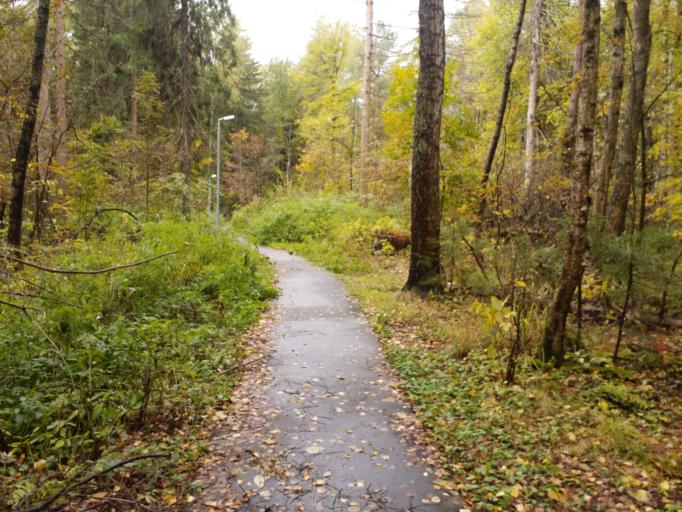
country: RU
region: Moskovskaya
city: Ashukino
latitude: 56.1623
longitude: 37.9563
